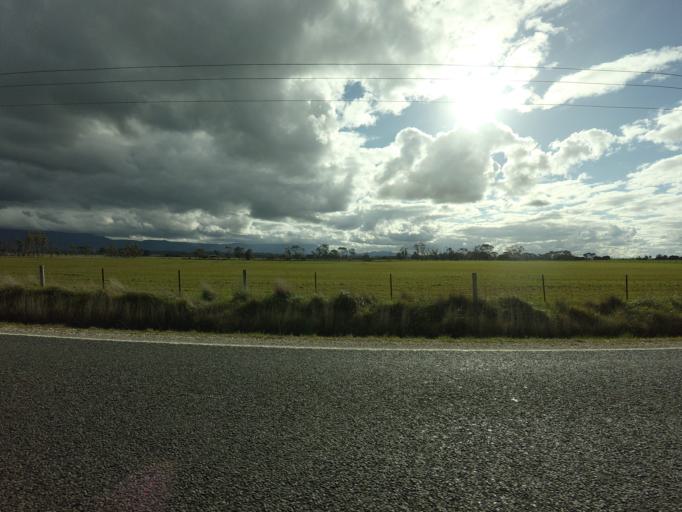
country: AU
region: Tasmania
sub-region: Northern Midlands
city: Longford
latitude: -41.7328
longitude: 147.0857
